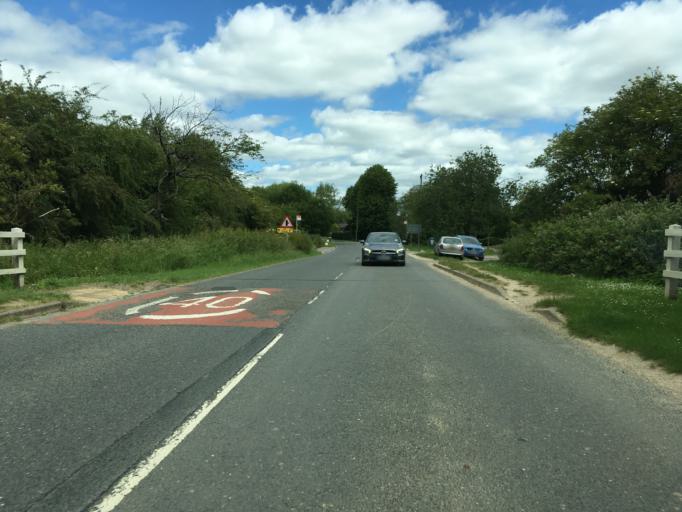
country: GB
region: England
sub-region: Hampshire
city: Overton
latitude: 51.2208
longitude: -1.3398
